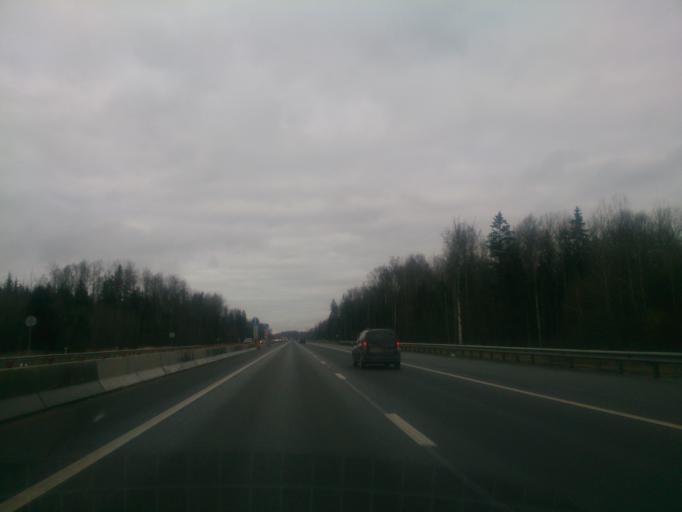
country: RU
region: Leningrad
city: Ul'yanovka
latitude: 59.5784
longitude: 30.7877
